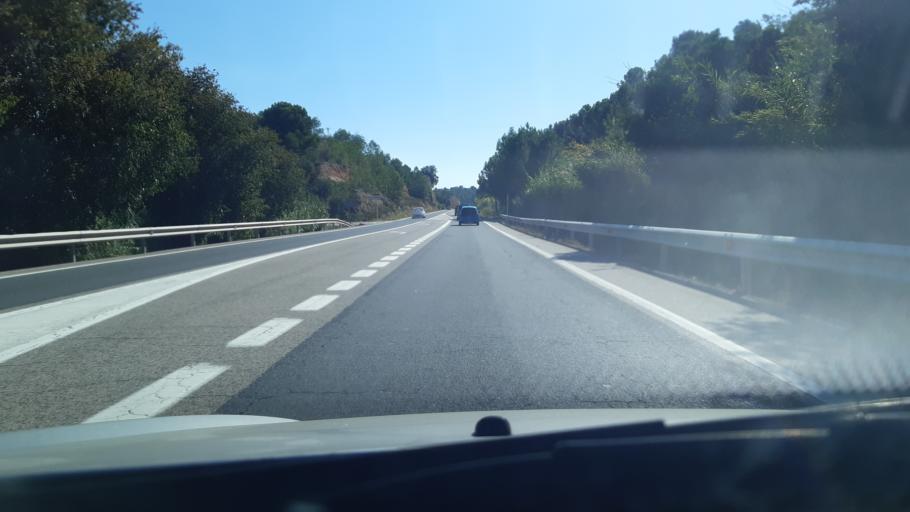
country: ES
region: Catalonia
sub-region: Provincia de Tarragona
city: Tivenys
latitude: 40.8903
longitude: 0.4904
